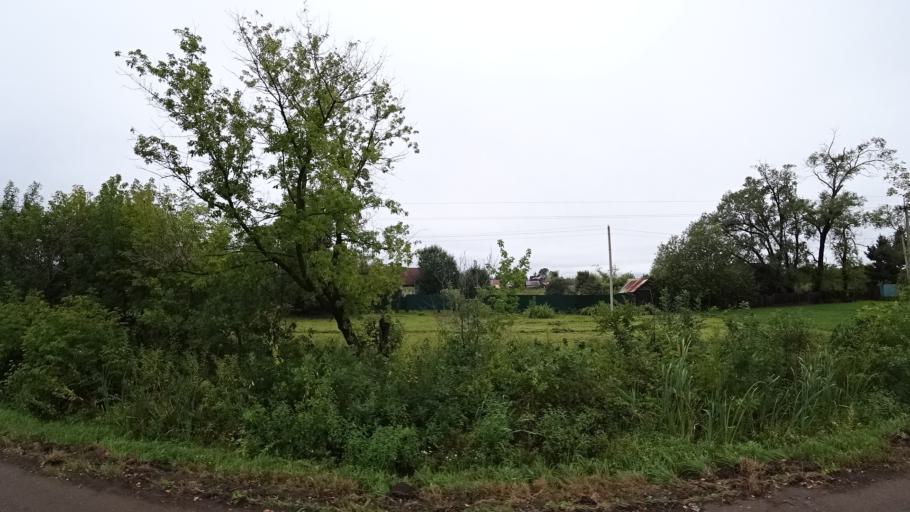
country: RU
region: Primorskiy
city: Monastyrishche
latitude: 44.2031
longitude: 132.4748
